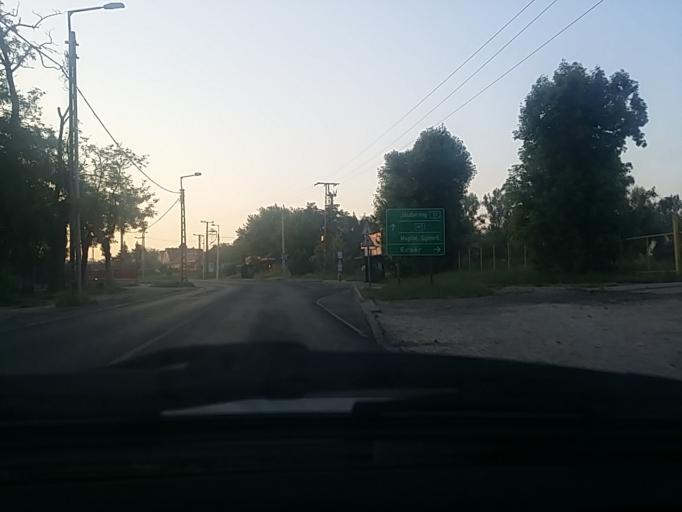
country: HU
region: Pest
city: Ecser
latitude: 47.4693
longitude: 19.2935
